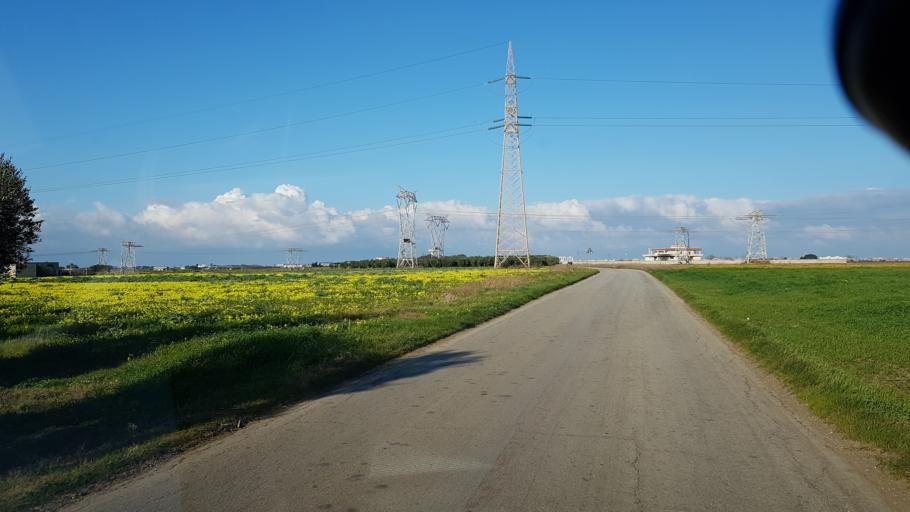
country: IT
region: Apulia
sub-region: Provincia di Brindisi
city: Brindisi
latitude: 40.5992
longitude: 17.9062
